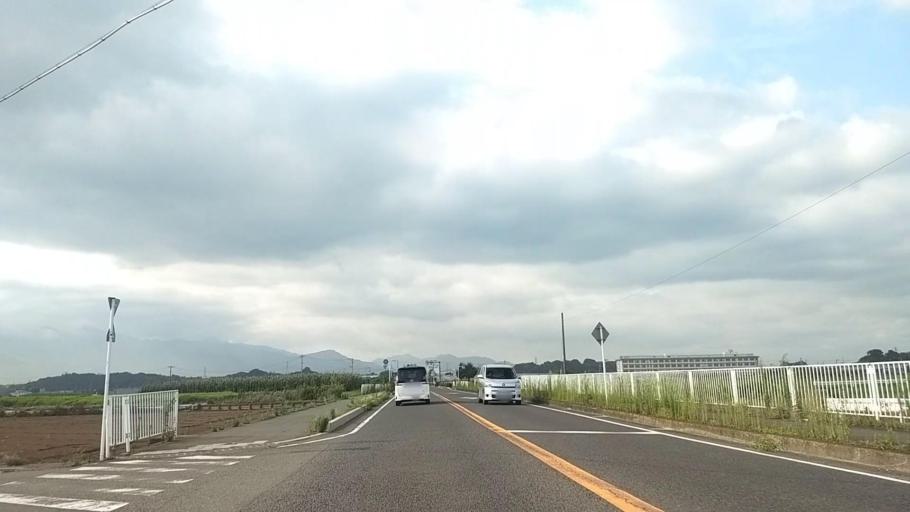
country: JP
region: Kanagawa
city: Isehara
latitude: 35.3665
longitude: 139.3231
